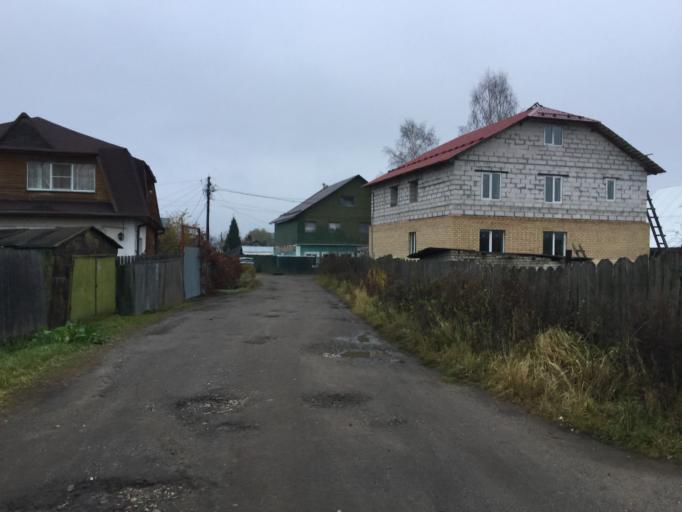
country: RU
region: Jaroslavl
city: Yaroslavl
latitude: 57.7209
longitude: 39.7718
